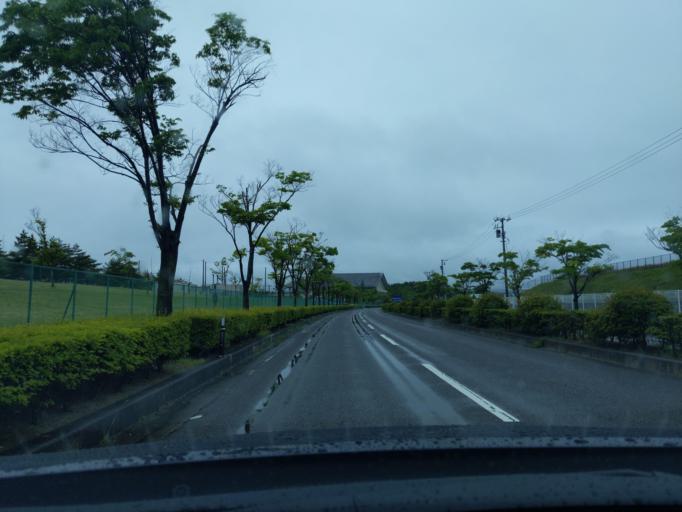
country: JP
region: Fukushima
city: Koriyama
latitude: 37.4471
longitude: 140.3187
